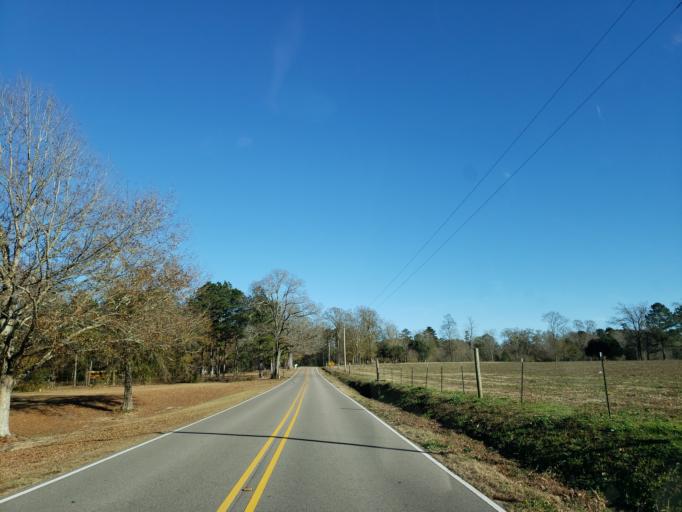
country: US
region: Mississippi
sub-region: Lamar County
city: Sumrall
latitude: 31.3550
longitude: -89.4803
